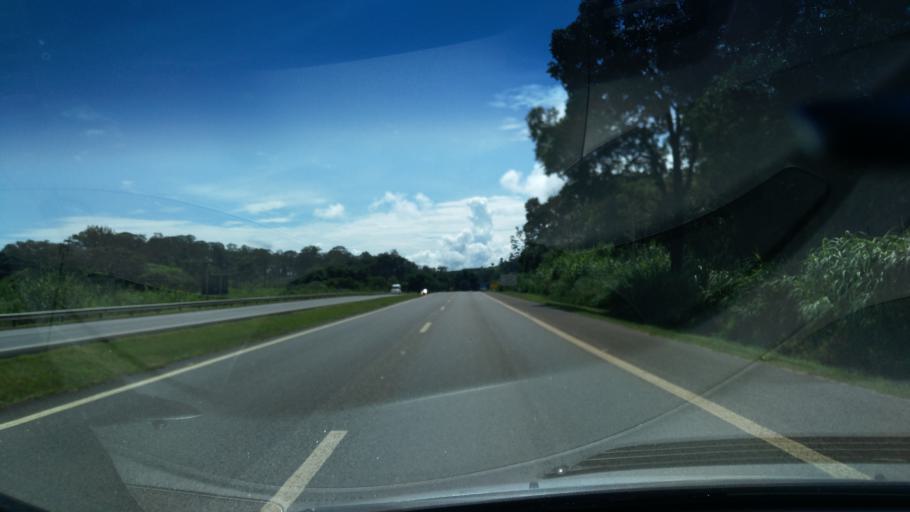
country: BR
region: Sao Paulo
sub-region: Santo Antonio Do Jardim
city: Espirito Santo do Pinhal
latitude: -22.2278
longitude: -46.7945
